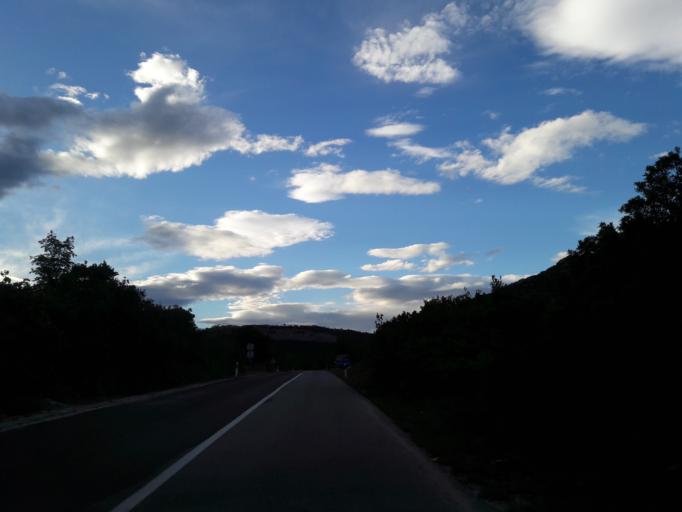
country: HR
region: Dubrovacko-Neretvanska
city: Ston
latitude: 42.8374
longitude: 17.6342
